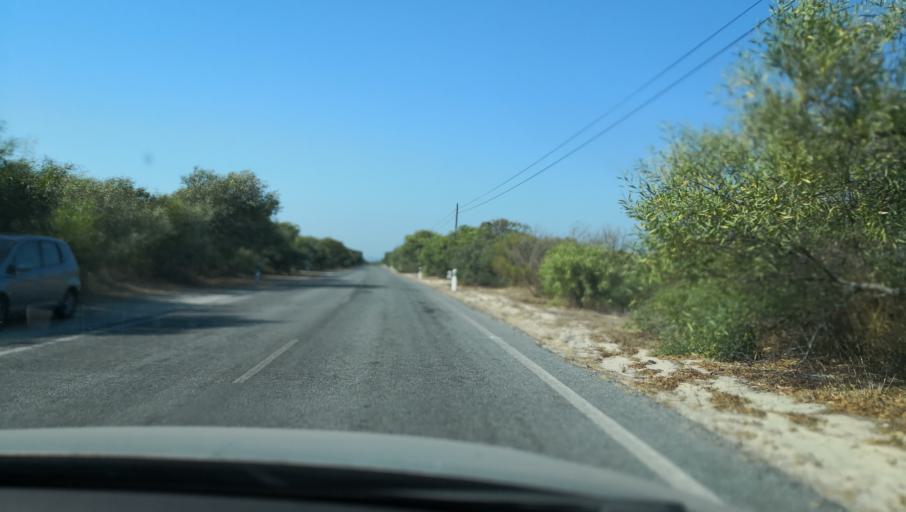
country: PT
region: Setubal
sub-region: Setubal
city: Setubal
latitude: 38.4029
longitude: -8.8075
